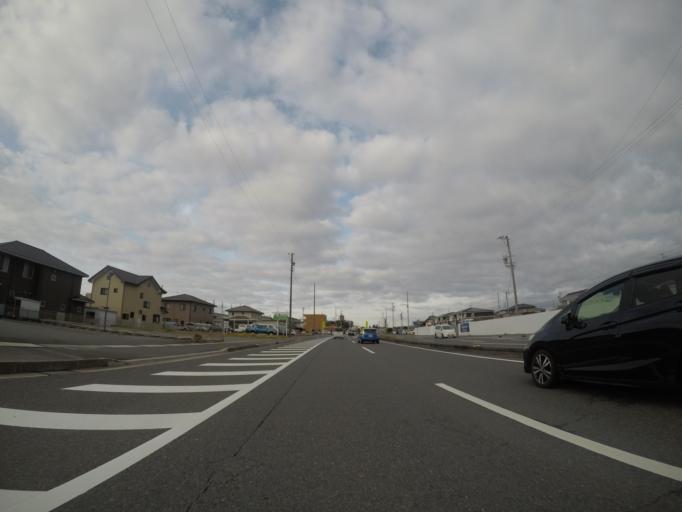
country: JP
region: Shizuoka
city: Hamakita
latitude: 34.8221
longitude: 137.8044
